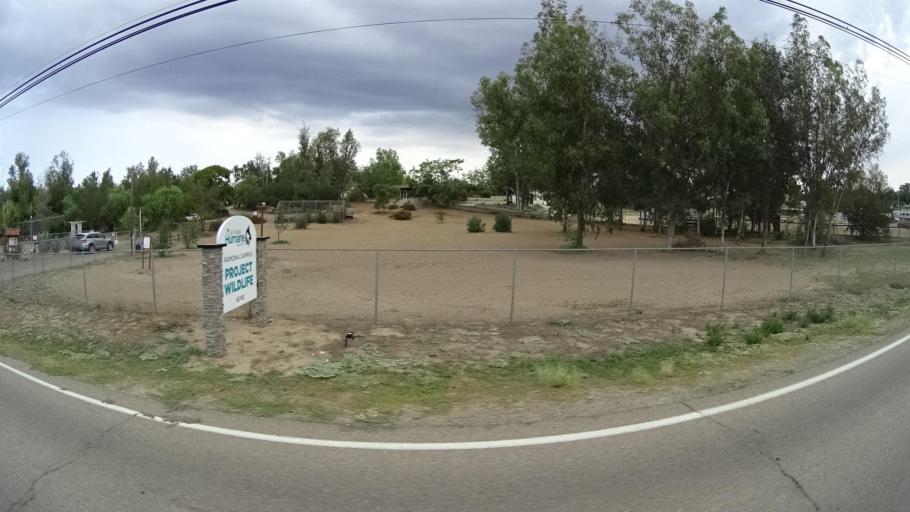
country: US
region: California
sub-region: San Diego County
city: Ramona
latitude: 33.0211
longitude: -116.9247
